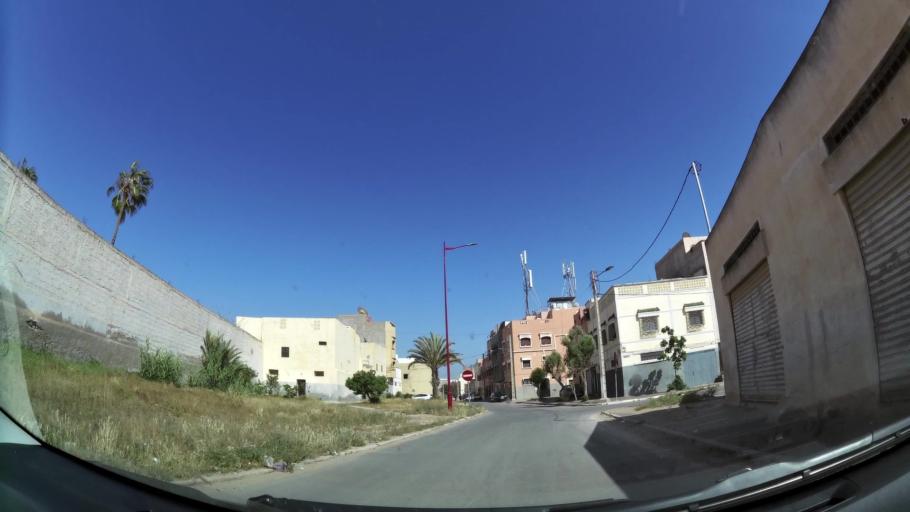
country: MA
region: Souss-Massa-Draa
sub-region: Inezgane-Ait Mellou
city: Inezgane
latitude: 30.3632
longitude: -9.5396
